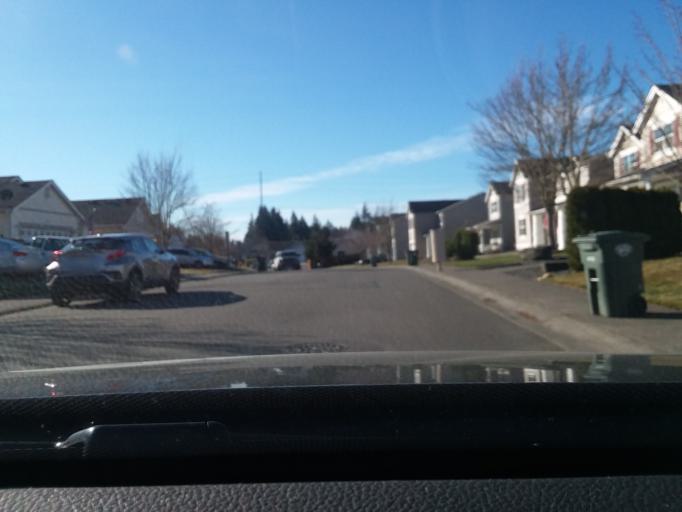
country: US
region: Washington
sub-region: Pierce County
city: Frederickson
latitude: 47.0982
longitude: -122.3158
